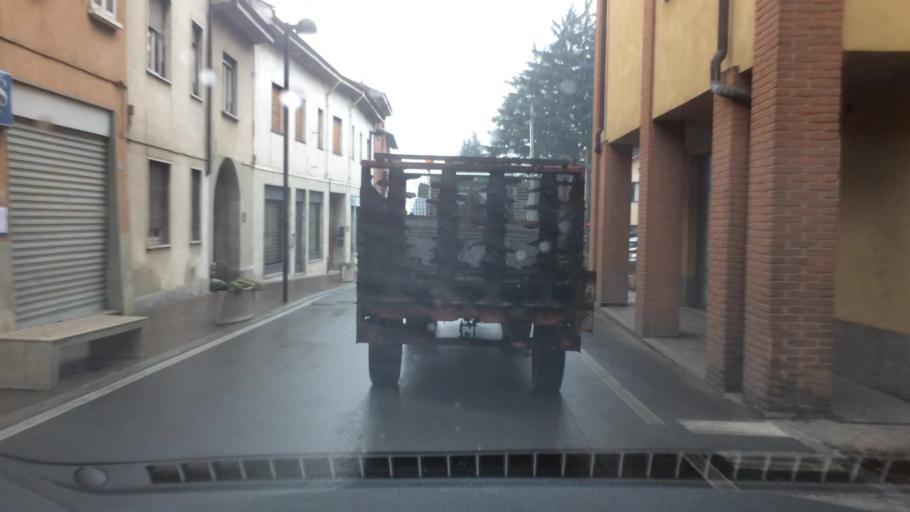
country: IT
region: Lombardy
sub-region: Provincia di Como
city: Bregnano
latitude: 45.6970
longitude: 9.0603
